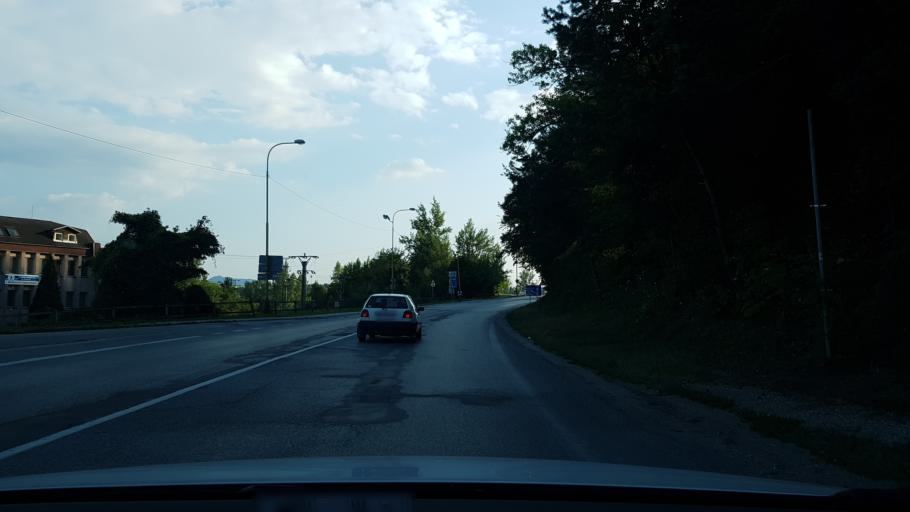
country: SK
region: Trenciansky
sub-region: Okres Povazska Bystrica
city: Povazska Bystrica
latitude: 49.1269
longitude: 18.4403
